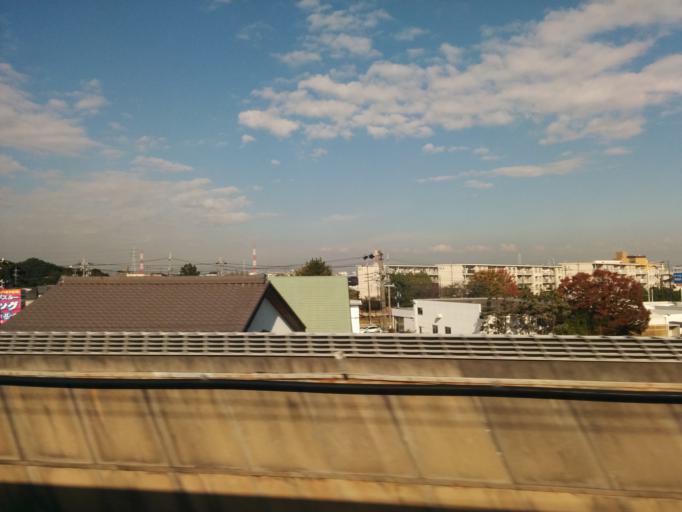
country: JP
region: Aichi
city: Chiryu
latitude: 35.0049
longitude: 137.0158
